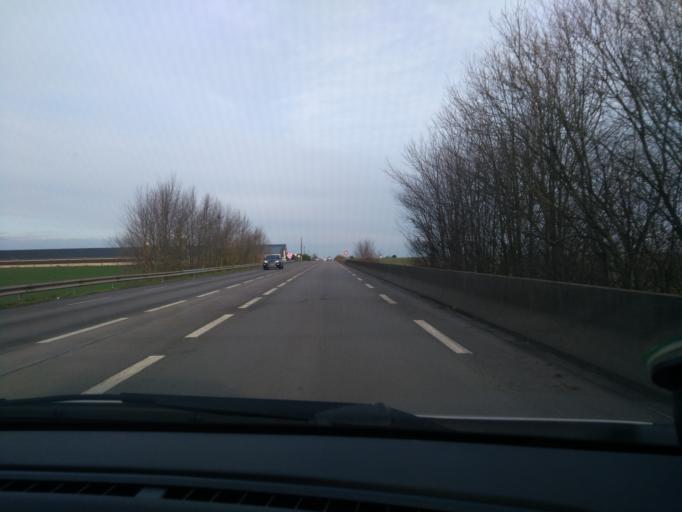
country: FR
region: Nord-Pas-de-Calais
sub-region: Departement du Nord
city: Maubeuge
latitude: 50.3228
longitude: 3.9757
